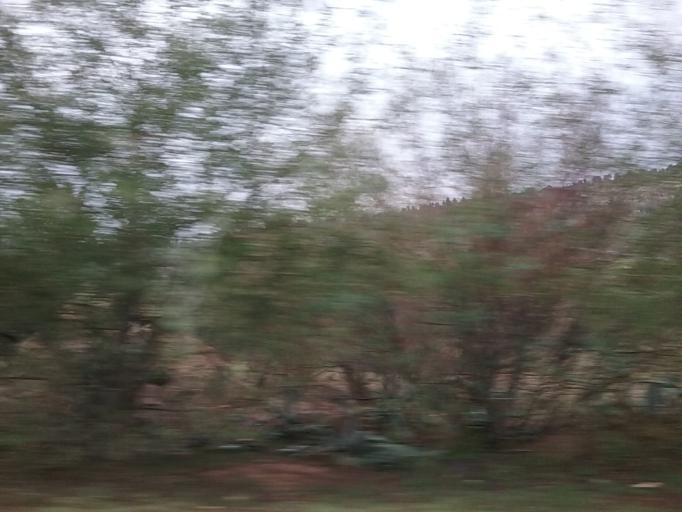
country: LS
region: Berea
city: Teyateyaneng
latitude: -29.1280
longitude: 27.7411
